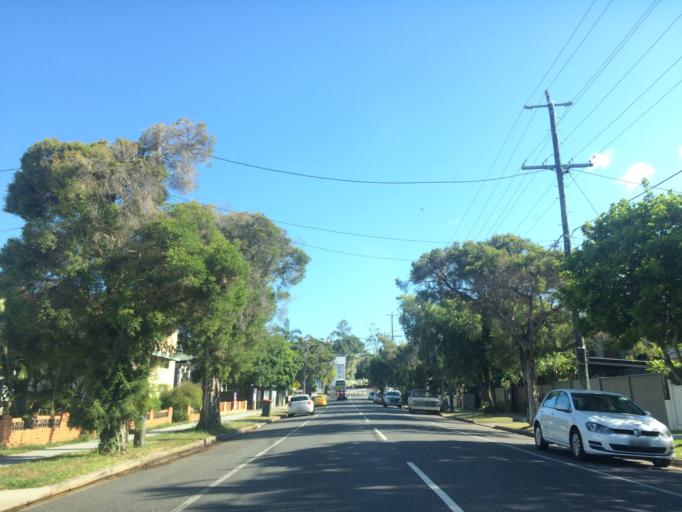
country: AU
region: Queensland
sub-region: Brisbane
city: Balmoral
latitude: -27.4537
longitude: 153.0619
